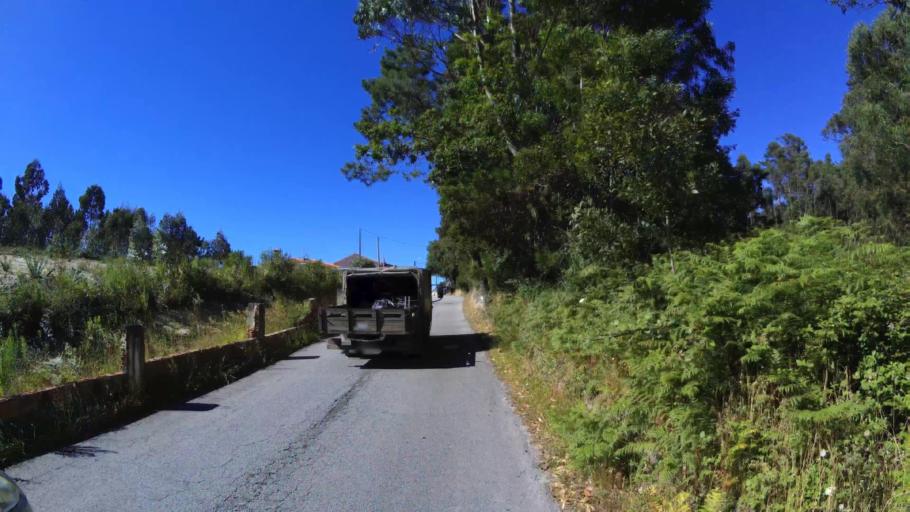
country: PT
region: Aveiro
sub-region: Aveiro
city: Aveiro
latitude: 40.6646
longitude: -8.6195
